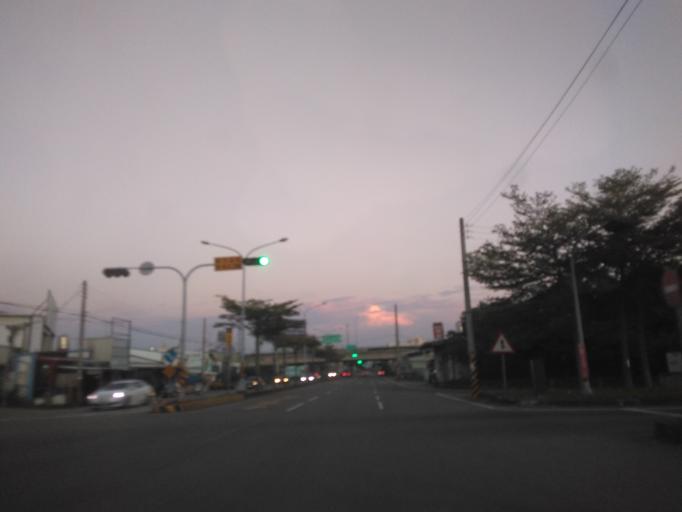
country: TW
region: Taiwan
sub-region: Changhua
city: Chang-hua
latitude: 24.0867
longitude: 120.5960
